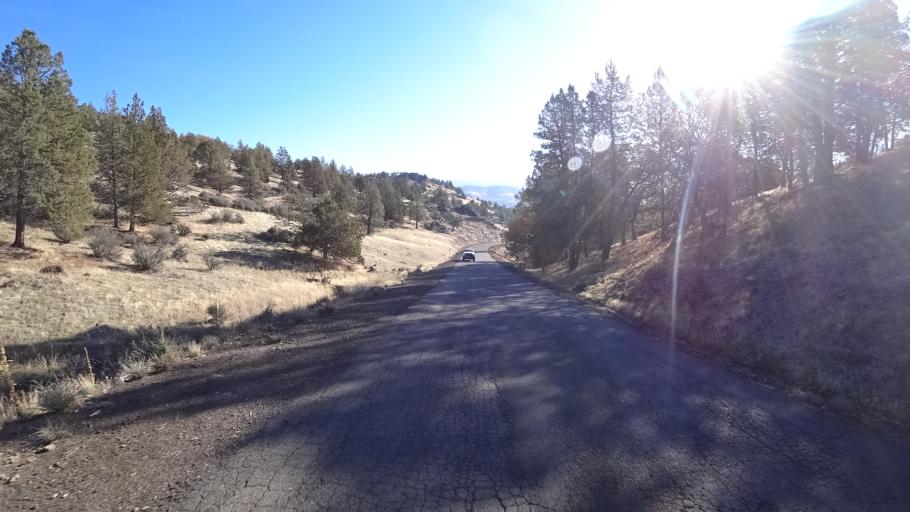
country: US
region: California
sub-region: Siskiyou County
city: Montague
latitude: 41.9022
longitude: -122.4282
